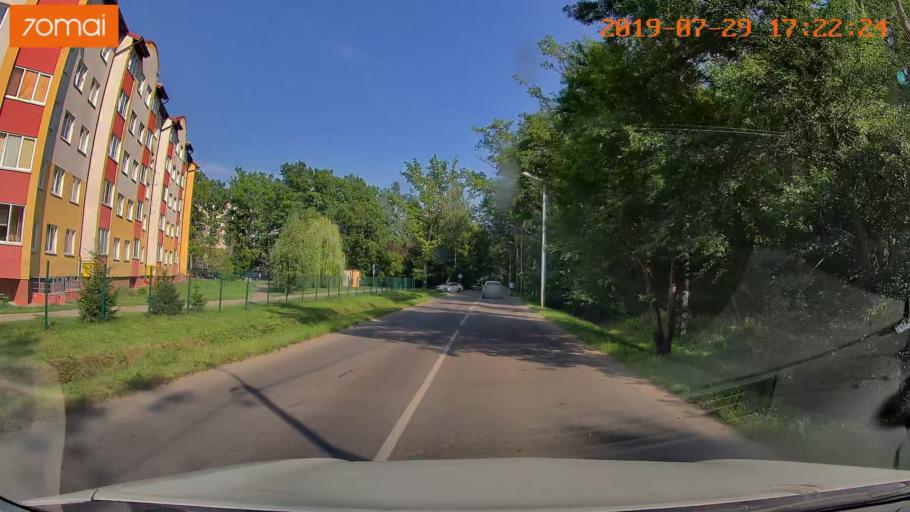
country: RU
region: Kaliningrad
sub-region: Gorod Kaliningrad
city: Kaliningrad
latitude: 54.7689
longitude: 20.4428
